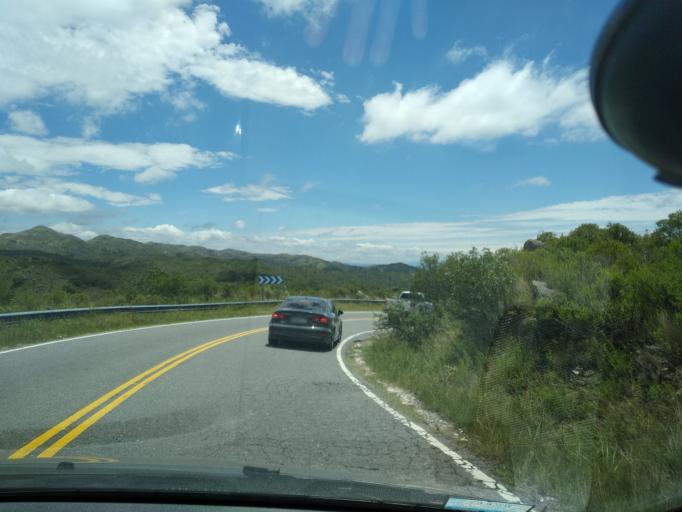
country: AR
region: Cordoba
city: Cuesta Blanca
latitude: -31.5923
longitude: -64.5273
